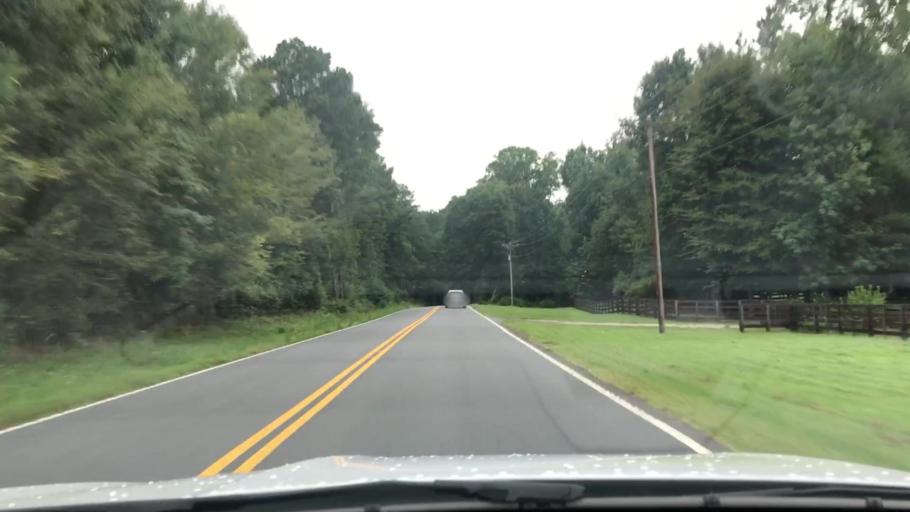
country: US
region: South Carolina
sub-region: Spartanburg County
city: Roebuck
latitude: 34.8336
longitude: -81.9627
